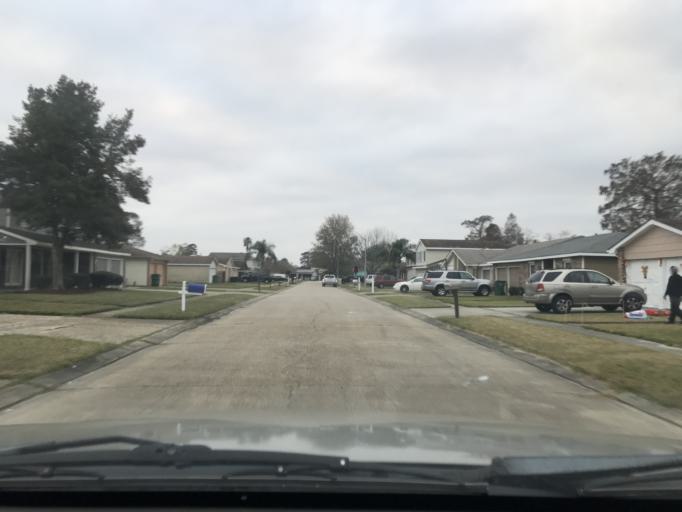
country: US
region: Louisiana
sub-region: Jefferson Parish
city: Woodmere
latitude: 29.8588
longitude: -90.0759
